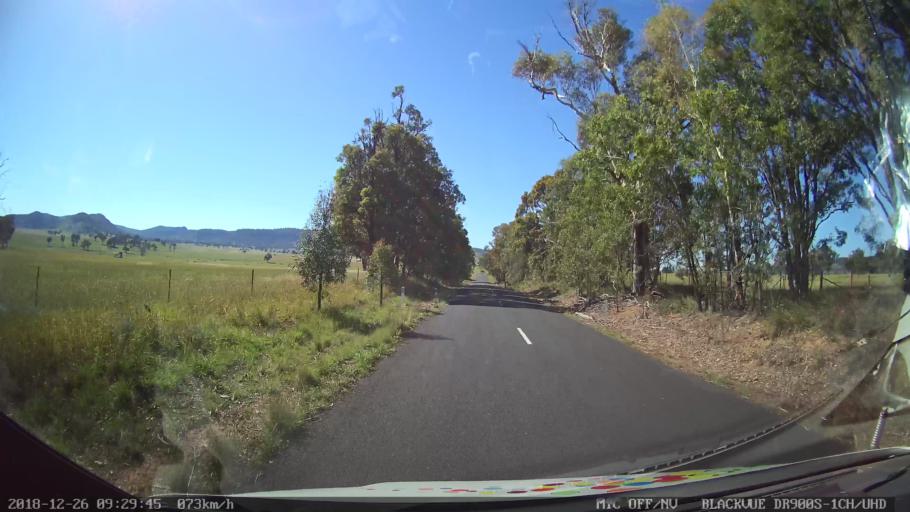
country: AU
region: New South Wales
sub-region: Mid-Western Regional
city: Kandos
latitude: -32.8561
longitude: 150.0288
